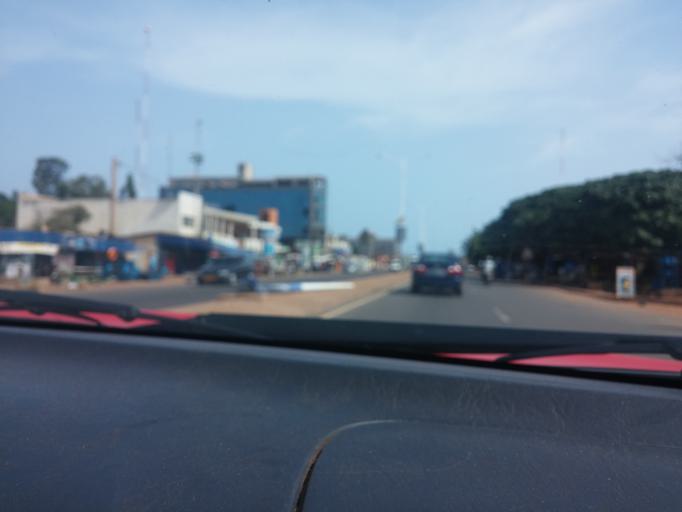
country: TG
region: Maritime
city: Lome
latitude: 6.2323
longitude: 1.2106
